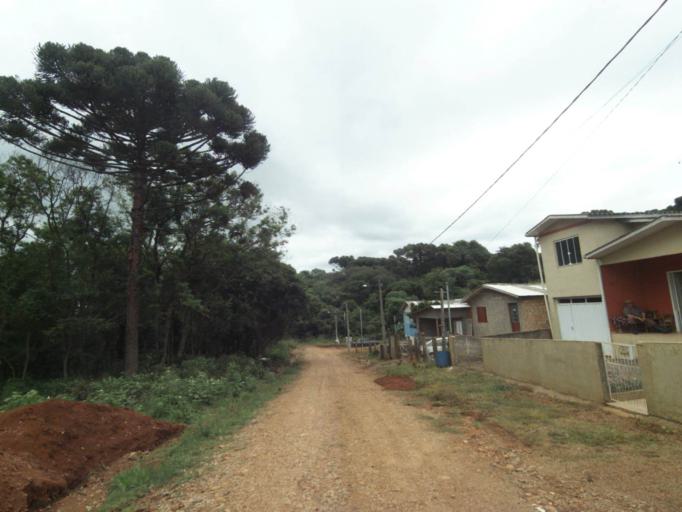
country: BR
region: Rio Grande do Sul
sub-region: Lagoa Vermelha
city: Lagoa Vermelha
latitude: -28.1949
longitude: -51.5294
